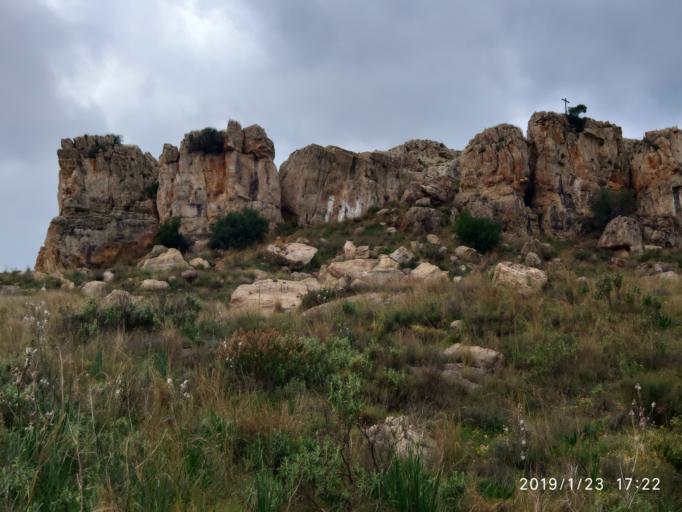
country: ES
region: Andalusia
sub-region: Provincia de Malaga
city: Malaga
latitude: 36.7376
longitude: -4.4370
